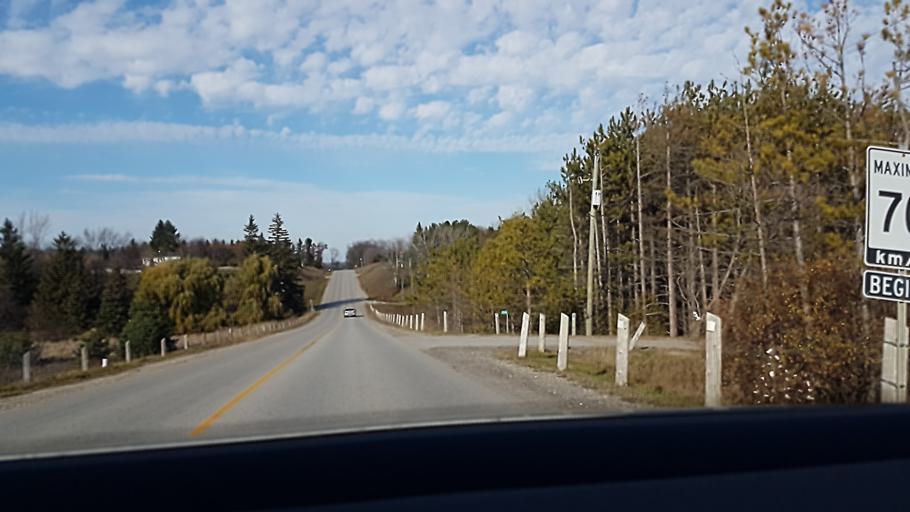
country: CA
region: Ontario
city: Bradford West Gwillimbury
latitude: 43.9942
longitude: -79.7589
